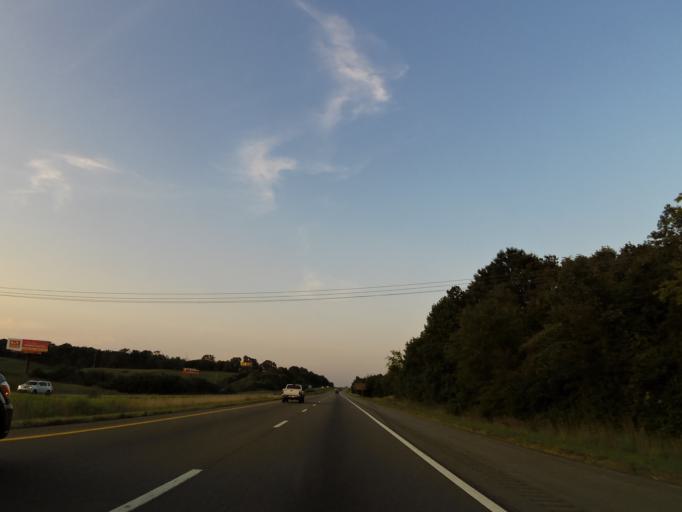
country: US
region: Tennessee
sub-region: Loudon County
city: Lenoir City
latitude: 35.8064
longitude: -84.3080
